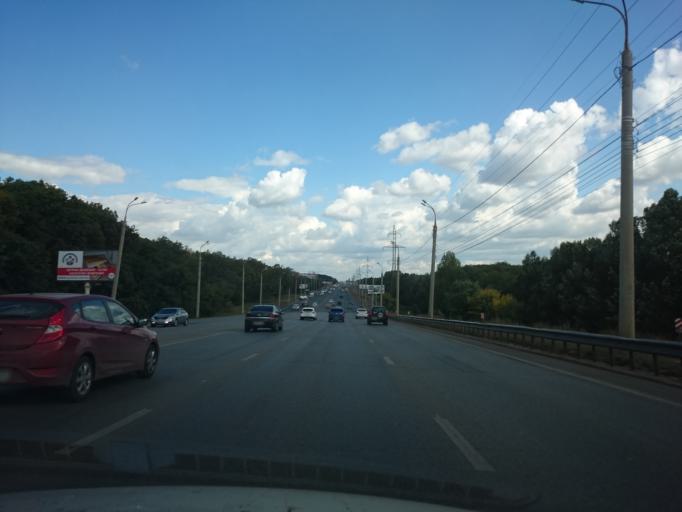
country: RU
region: Samara
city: Samara
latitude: 53.2662
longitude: 50.2485
